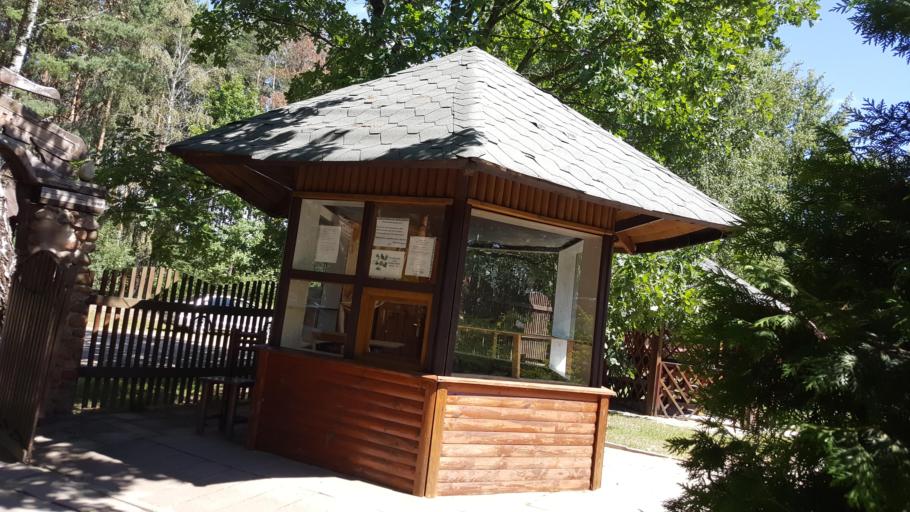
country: BY
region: Brest
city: Kobryn
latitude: 52.3488
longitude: 24.3212
